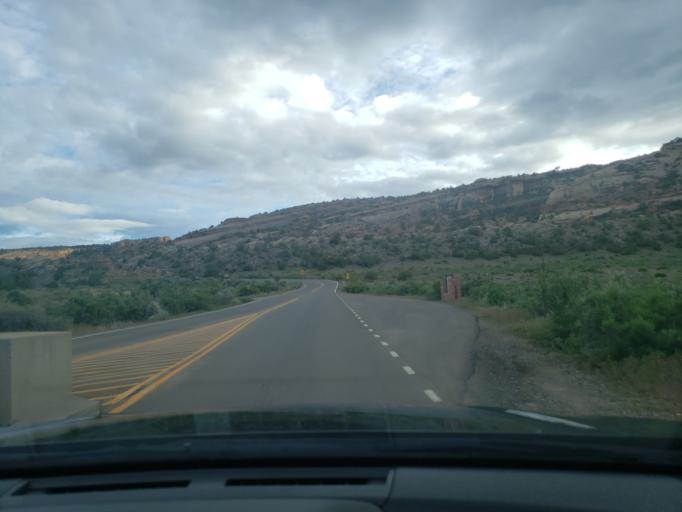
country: US
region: Colorado
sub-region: Mesa County
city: Redlands
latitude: 39.0350
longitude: -108.6311
